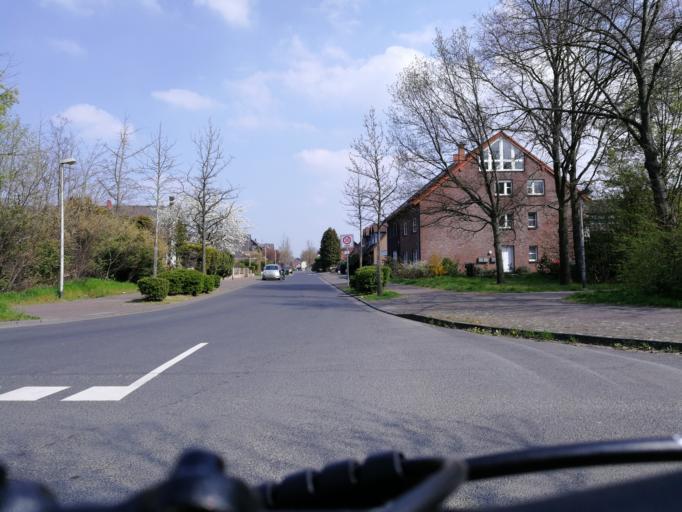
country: DE
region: North Rhine-Westphalia
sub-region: Regierungsbezirk Dusseldorf
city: Dormagen
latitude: 51.1369
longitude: 6.8075
